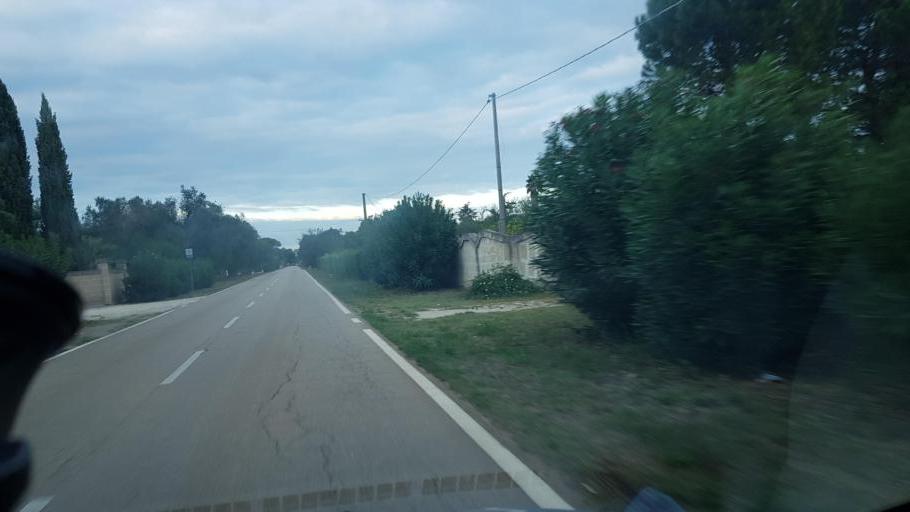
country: IT
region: Apulia
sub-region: Provincia di Brindisi
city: Latiano
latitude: 40.5357
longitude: 17.6910
